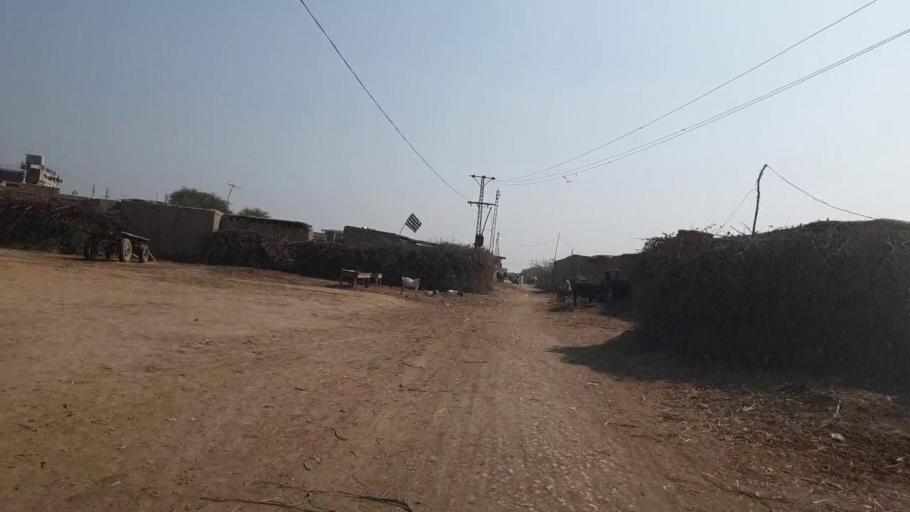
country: PK
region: Sindh
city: Bhit Shah
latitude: 25.7284
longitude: 68.5329
